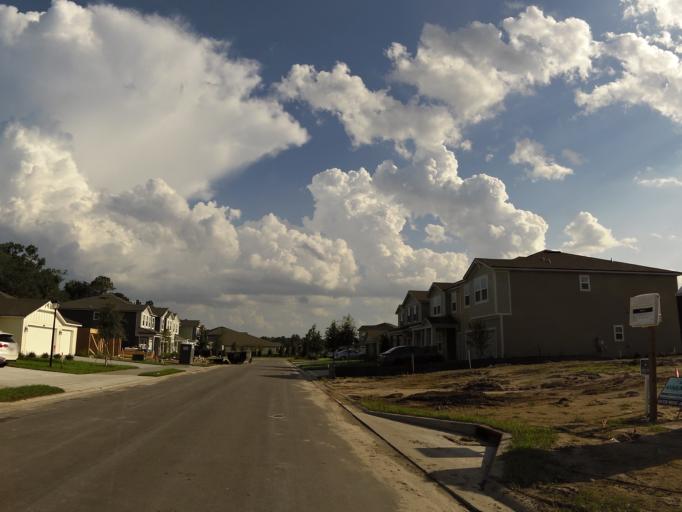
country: US
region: Florida
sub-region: Clay County
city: Green Cove Springs
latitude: 30.0306
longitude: -81.6292
